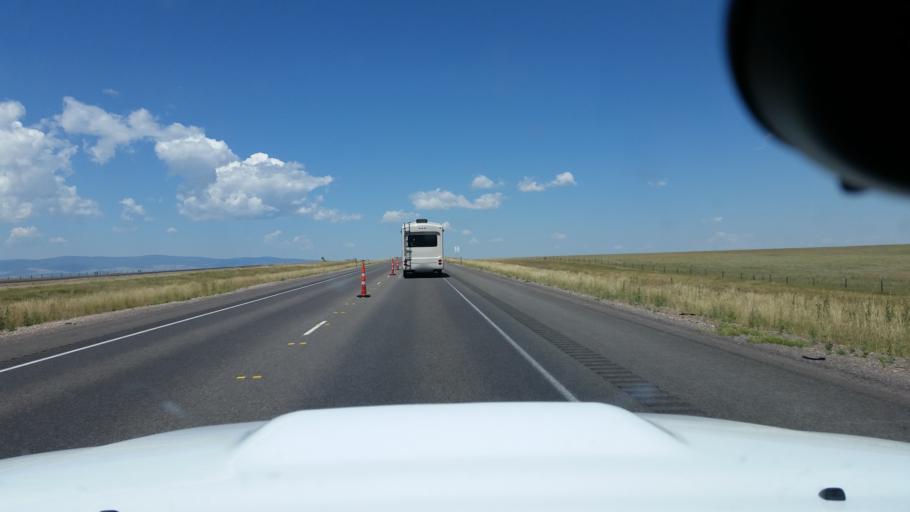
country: US
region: Wyoming
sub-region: Albany County
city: Laramie
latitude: 41.3660
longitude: -105.7811
